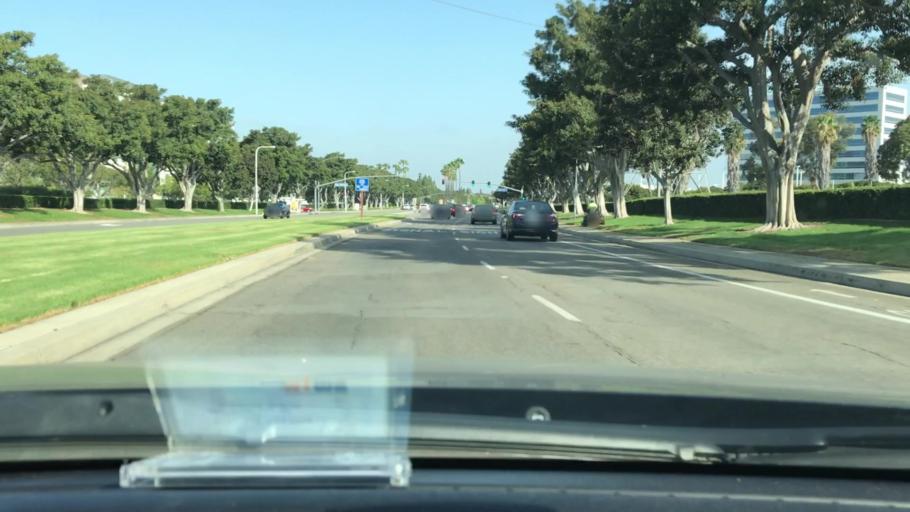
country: US
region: California
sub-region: Orange County
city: Irvine
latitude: 33.6576
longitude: -117.7713
